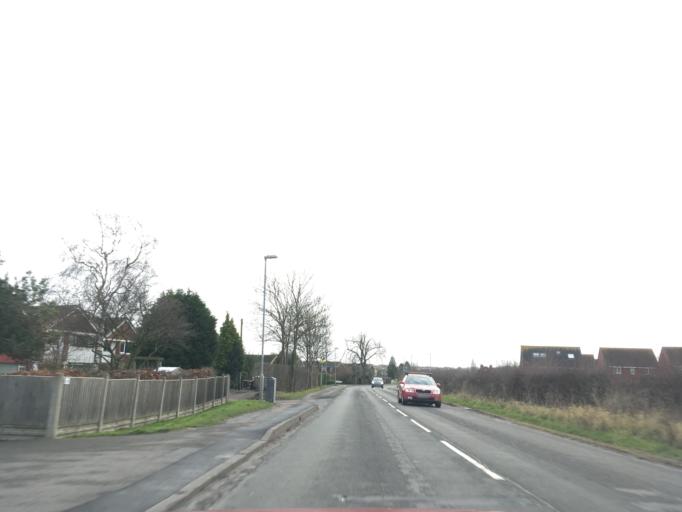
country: GB
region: England
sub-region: Nottinghamshire
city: East Leake
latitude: 52.8421
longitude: -1.1801
